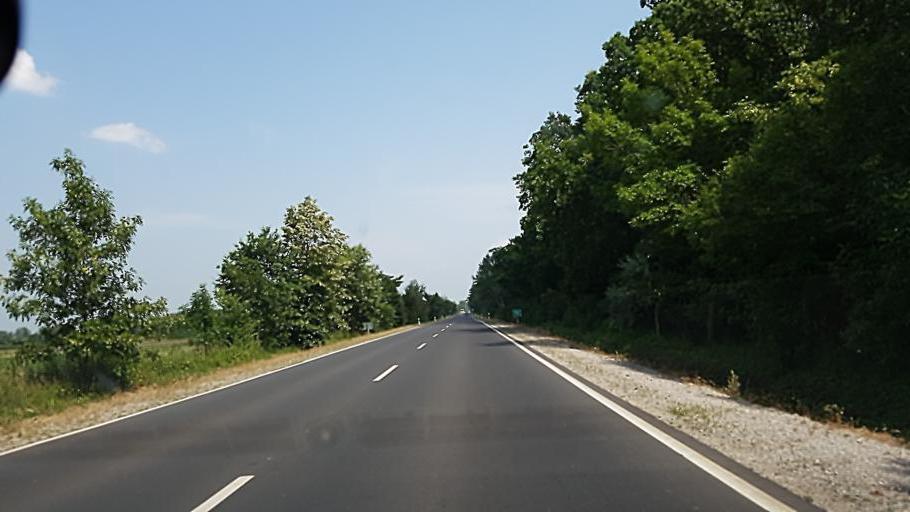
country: HU
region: Heves
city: Besenyotelek
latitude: 47.6758
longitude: 20.5262
